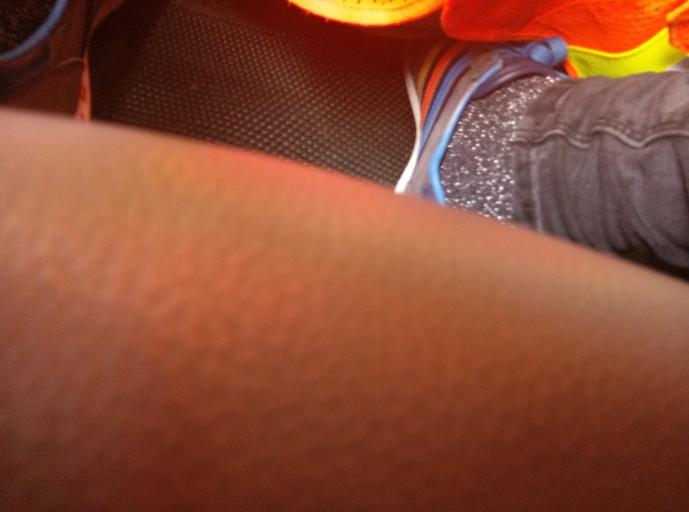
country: CD
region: Nord Kivu
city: Goma
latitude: -1.6740
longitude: 29.2459
